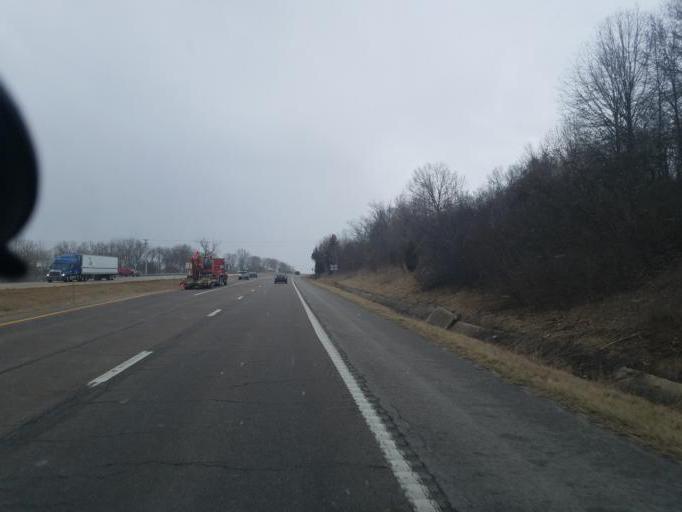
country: US
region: Missouri
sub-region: Boone County
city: Hallsville
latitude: 39.1209
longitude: -92.3312
